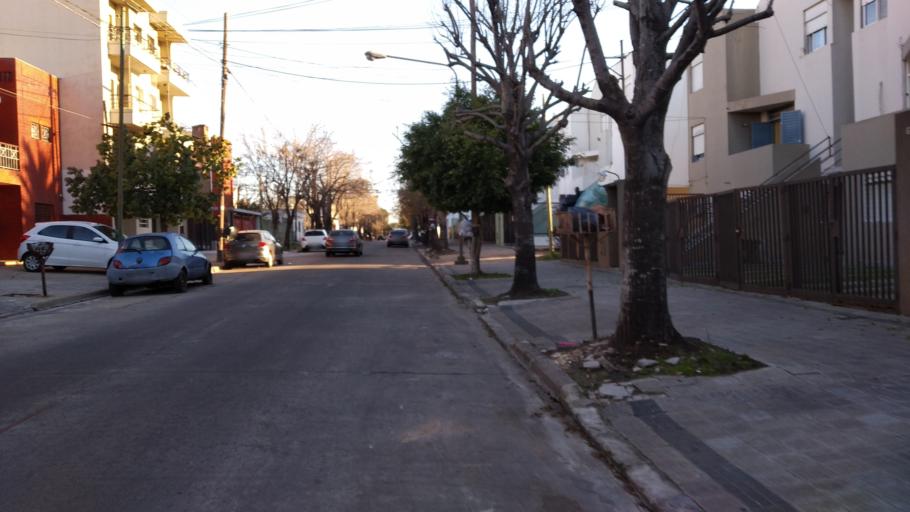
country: AR
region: Buenos Aires
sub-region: Partido de La Plata
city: La Plata
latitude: -34.9195
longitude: -57.9876
